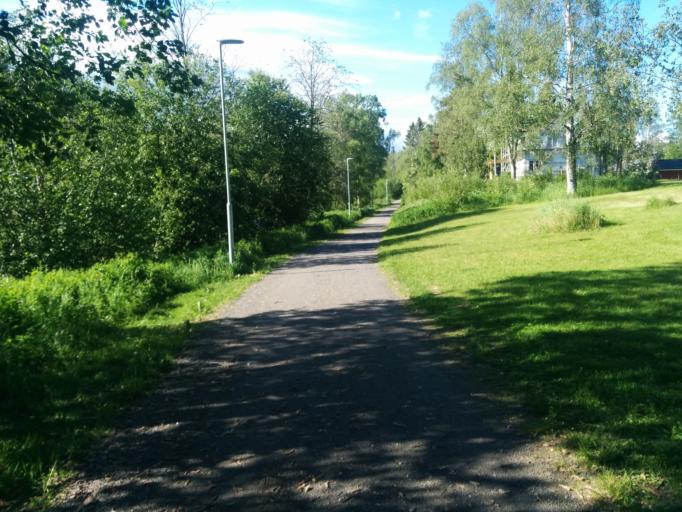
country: SE
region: Vaesterbotten
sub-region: Umea Kommun
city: Hoernefors
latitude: 63.6302
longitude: 19.9117
